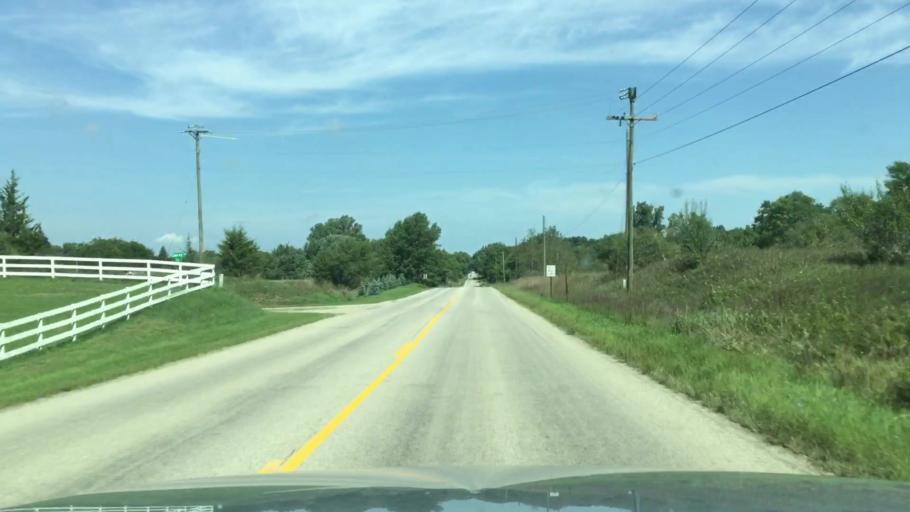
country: US
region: Michigan
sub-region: Lenawee County
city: Manitou Beach-Devils Lake
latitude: 42.0335
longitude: -84.2763
